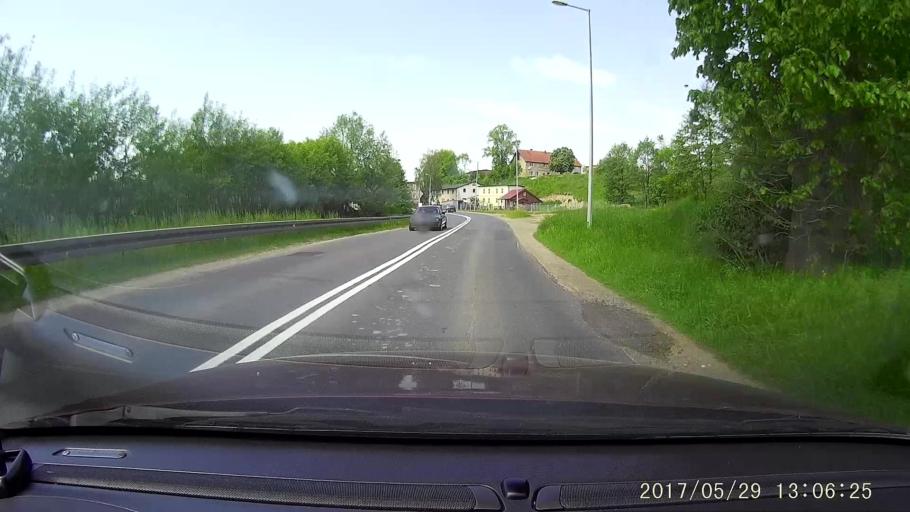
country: PL
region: Lower Silesian Voivodeship
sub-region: Powiat jeleniogorski
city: Stara Kamienica
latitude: 50.9511
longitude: 15.5815
